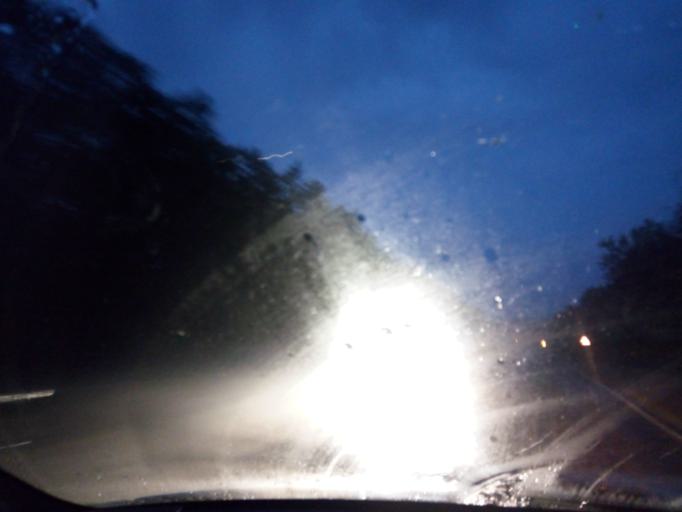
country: RU
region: Primorskiy
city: Dal'nerechensk
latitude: 45.8946
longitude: 133.7356
